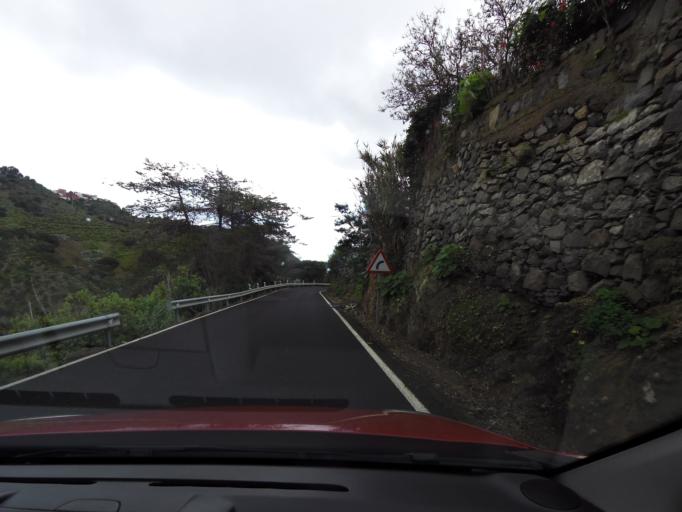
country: ES
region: Canary Islands
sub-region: Provincia de Las Palmas
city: Santa Brigida
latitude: 28.0252
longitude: -15.4726
